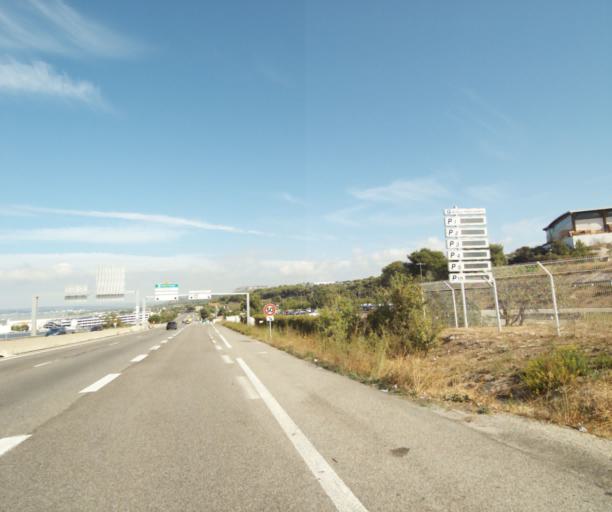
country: FR
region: Provence-Alpes-Cote d'Azur
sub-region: Departement des Bouches-du-Rhone
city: Saint-Victoret
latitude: 43.4313
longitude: 5.2348
